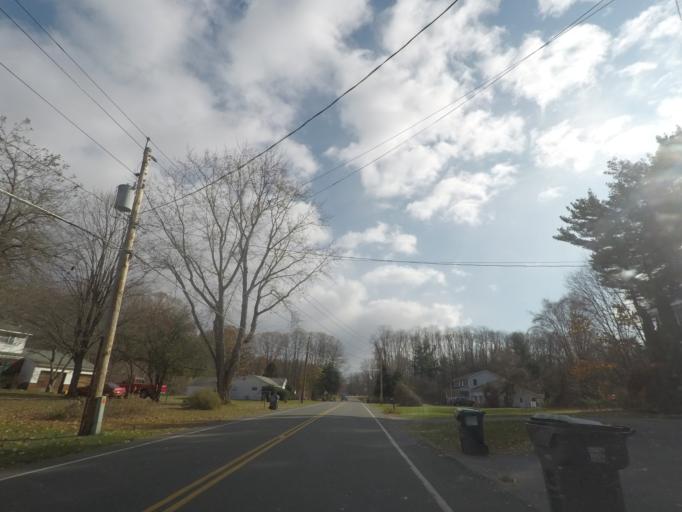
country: US
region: New York
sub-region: Saratoga County
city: Country Knolls
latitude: 42.9155
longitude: -73.8306
